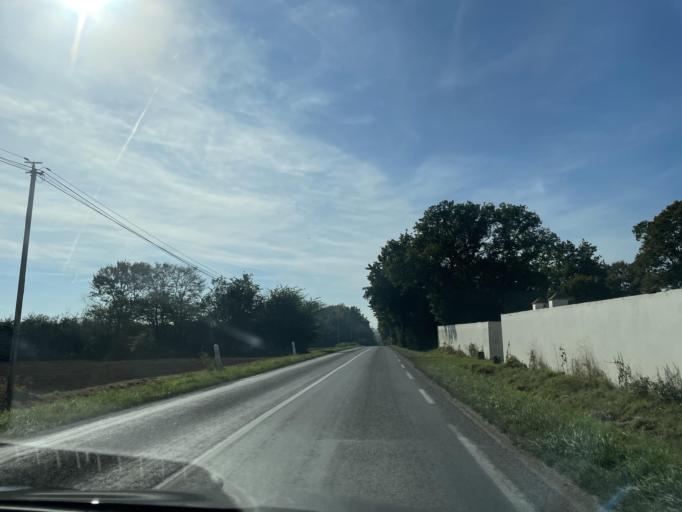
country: FR
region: Ile-de-France
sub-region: Departement de Seine-et-Marne
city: Coulommiers
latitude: 48.8490
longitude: 3.0901
